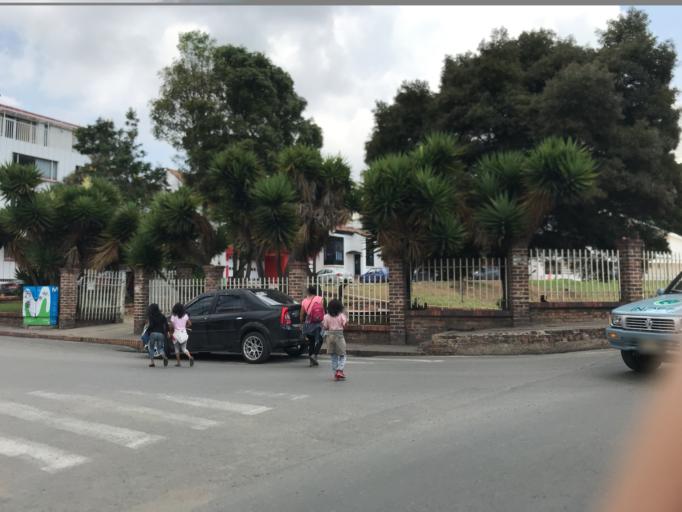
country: CO
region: Boyaca
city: Tunja
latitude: 5.5370
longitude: -73.3614
